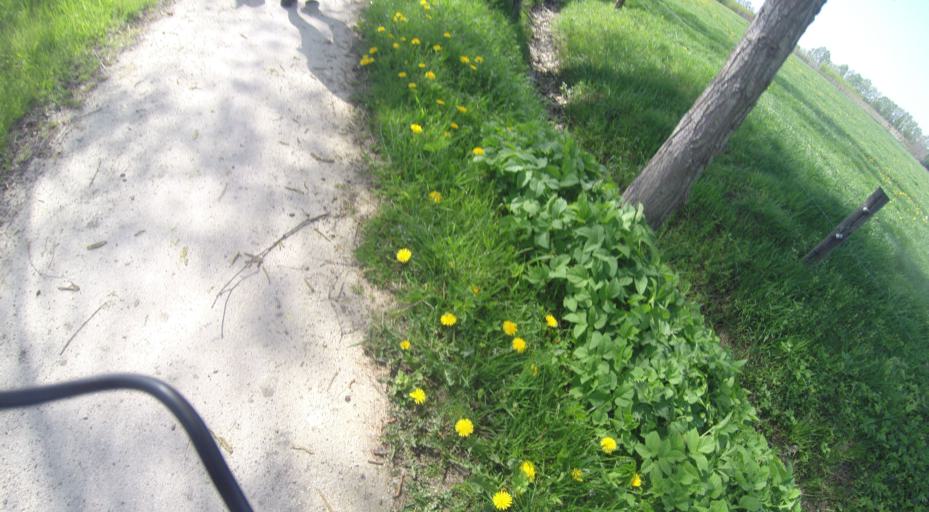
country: NL
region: Gelderland
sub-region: Oost Gelre
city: Lichtenvoorde
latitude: 52.0022
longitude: 6.5302
